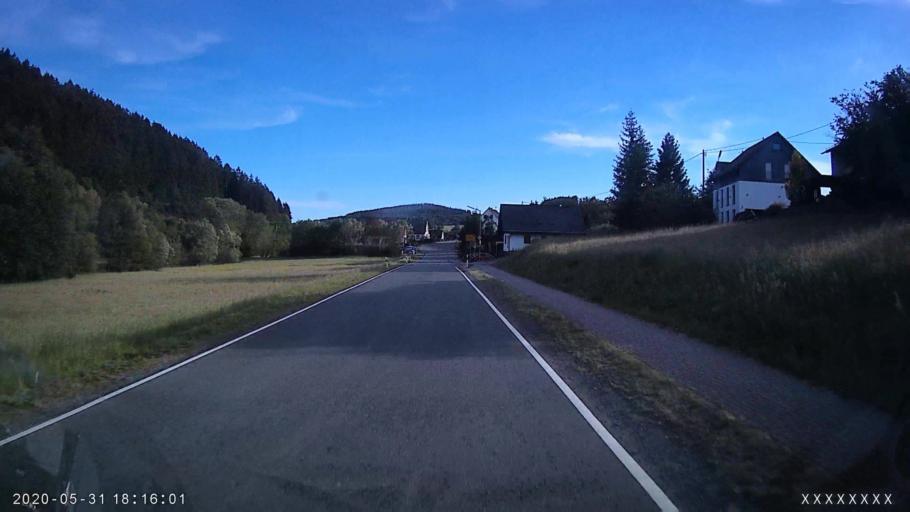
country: DE
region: Hesse
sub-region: Regierungsbezirk Giessen
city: Haiger
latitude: 50.8109
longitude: 8.2046
